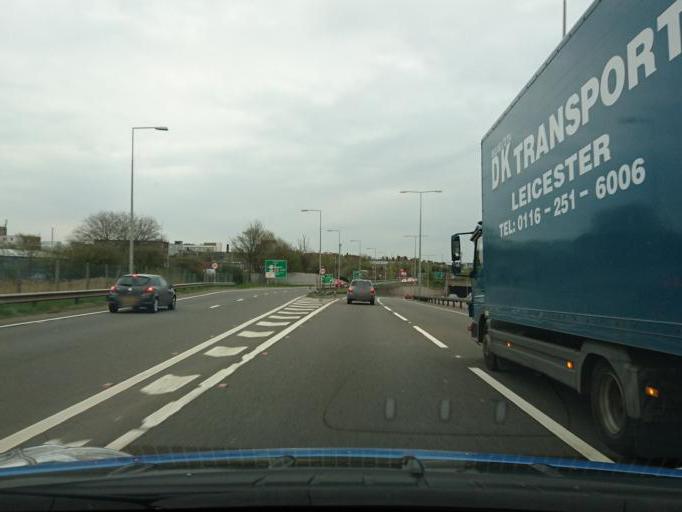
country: GB
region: England
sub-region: Stoke-on-Trent
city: Stoke-on-Trent
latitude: 53.0101
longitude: -2.1884
